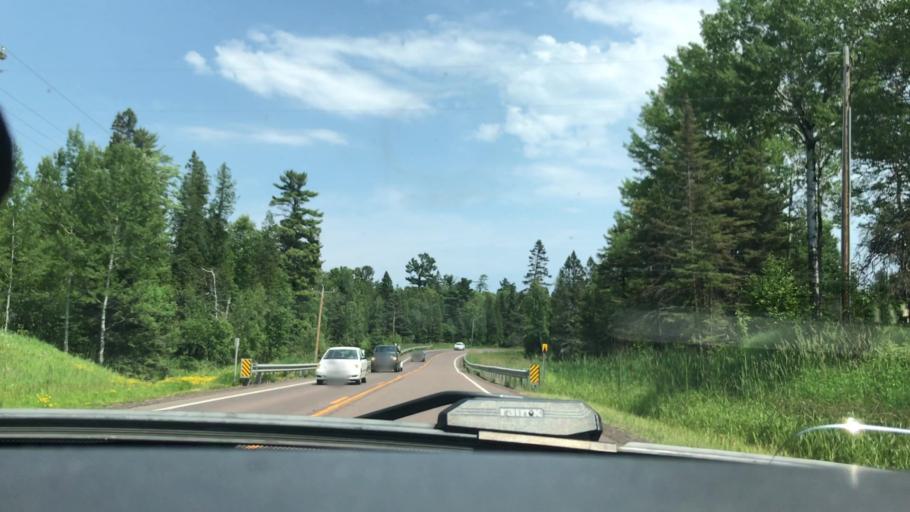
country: US
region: Minnesota
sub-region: Lake County
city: Two Harbors
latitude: 47.0962
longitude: -91.5653
